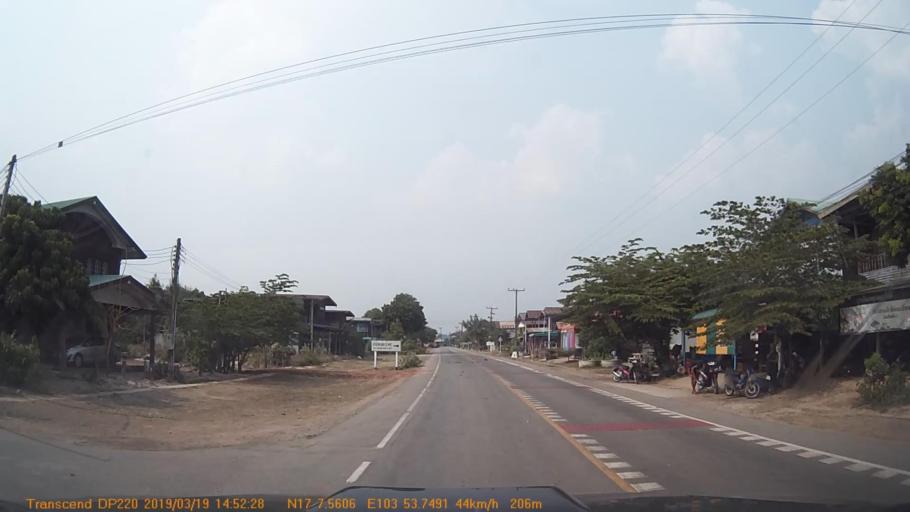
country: TH
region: Sakon Nakhon
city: Kut Bak
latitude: 17.1261
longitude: 103.8958
